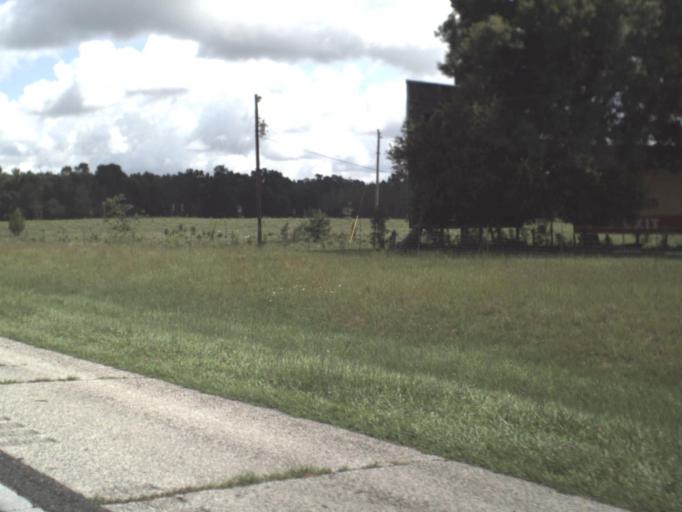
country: US
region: Florida
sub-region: Alachua County
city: High Springs
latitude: 29.9200
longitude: -82.5557
